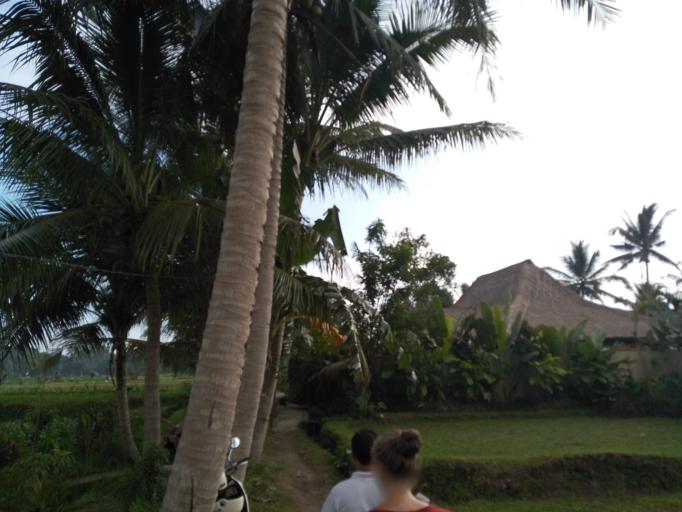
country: ID
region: Bali
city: Banjar Pande
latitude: -8.4958
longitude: 115.2474
